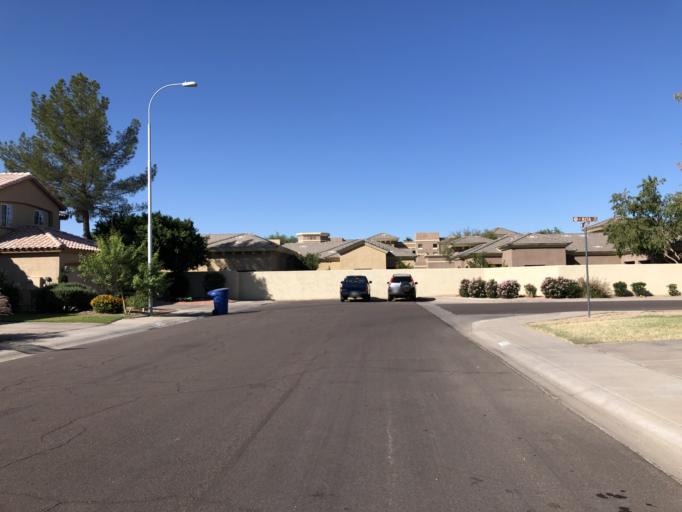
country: US
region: Arizona
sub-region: Maricopa County
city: Guadalupe
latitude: 33.3067
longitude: -111.9245
